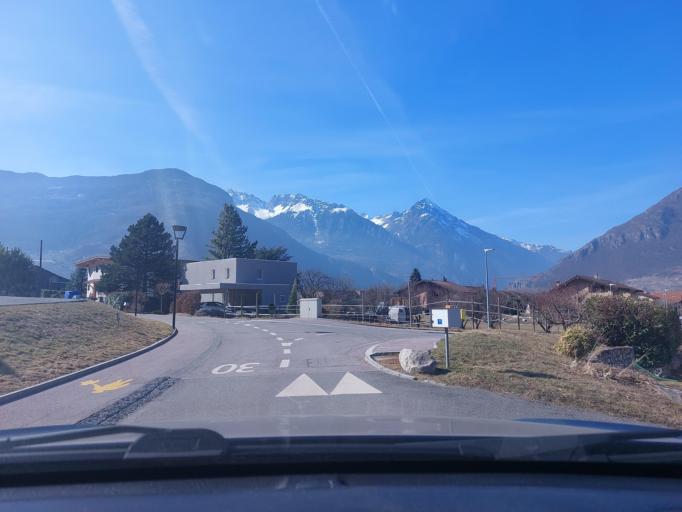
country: CH
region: Valais
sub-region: Martigny District
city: Martigny-Ville
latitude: 46.1036
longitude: 7.0988
